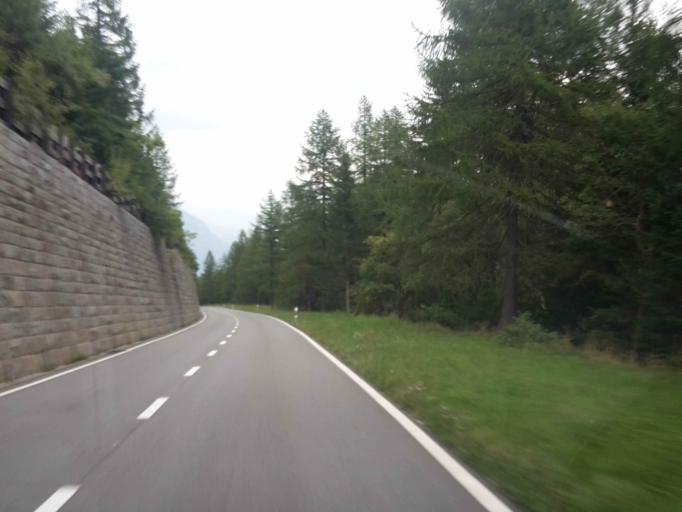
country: CH
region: Valais
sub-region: Martigny District
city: Martigny-Combe
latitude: 46.0639
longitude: 7.0129
